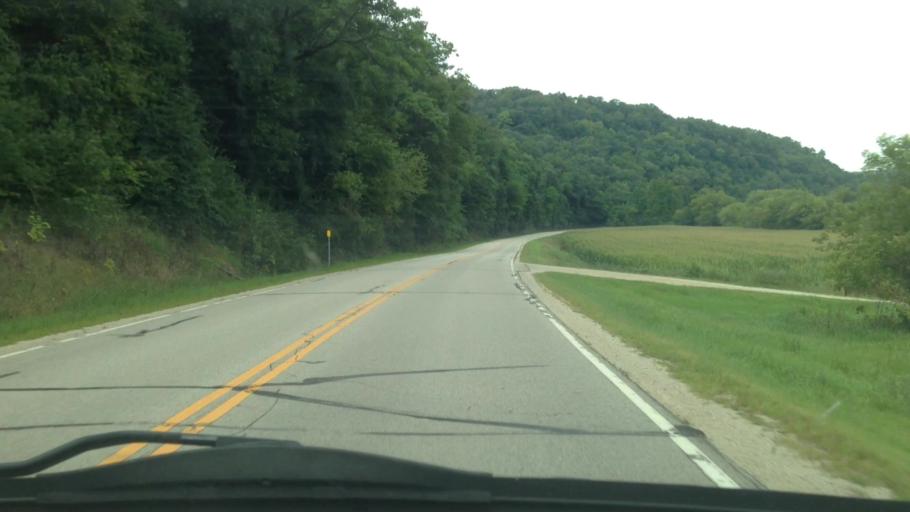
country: US
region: Minnesota
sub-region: Fillmore County
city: Preston
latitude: 43.7274
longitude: -91.9641
